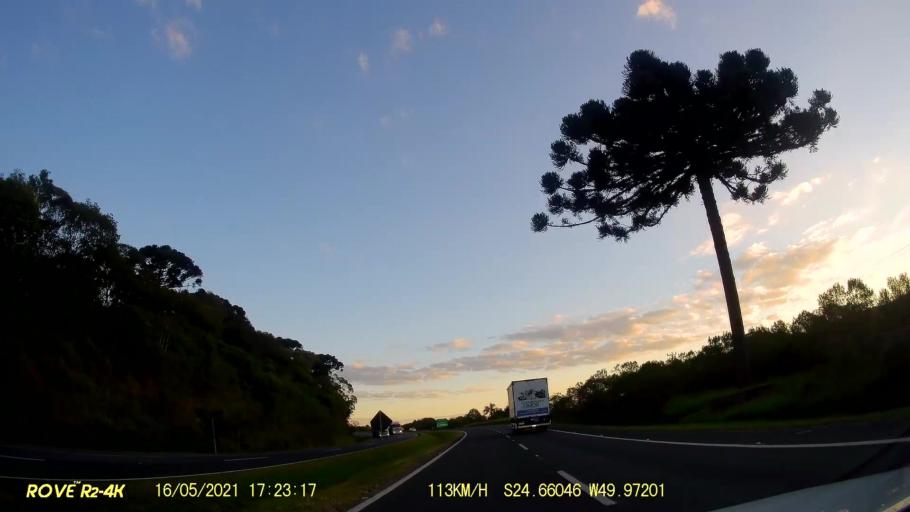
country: BR
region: Parana
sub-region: Castro
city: Castro
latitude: -24.6613
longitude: -49.9724
